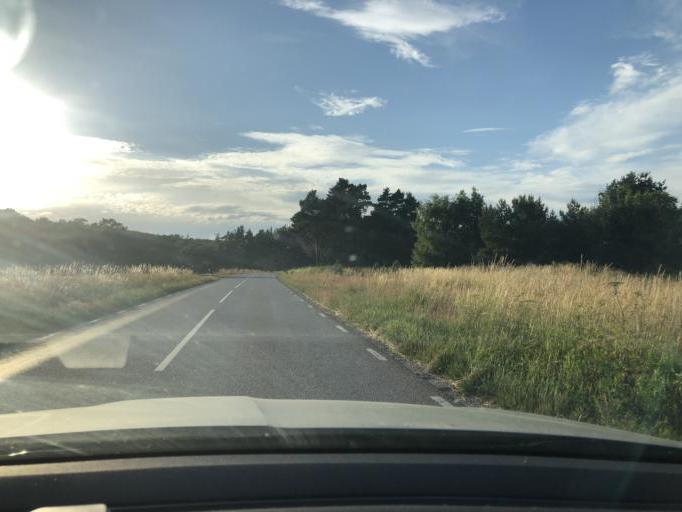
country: SE
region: Blekinge
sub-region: Solvesborgs Kommun
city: Soelvesborg
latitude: 56.0760
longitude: 14.6103
